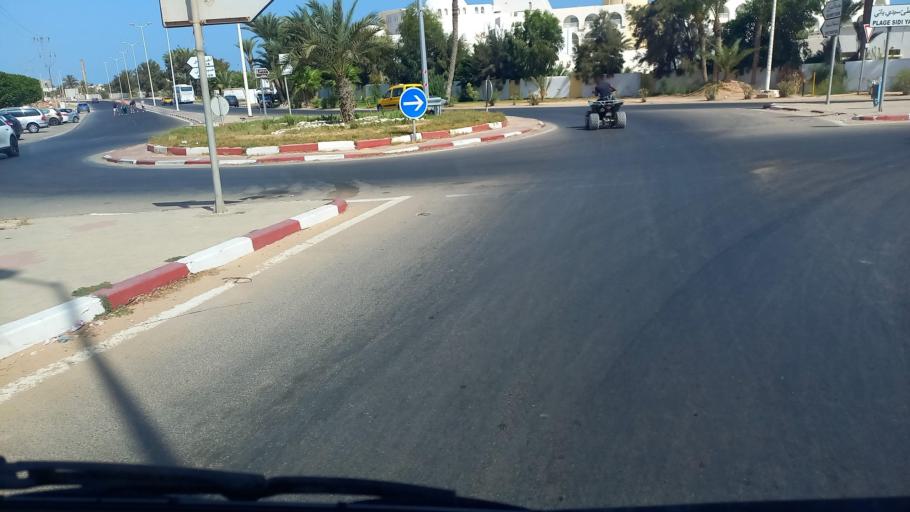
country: TN
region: Madanin
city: Midoun
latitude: 33.8242
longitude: 11.0413
